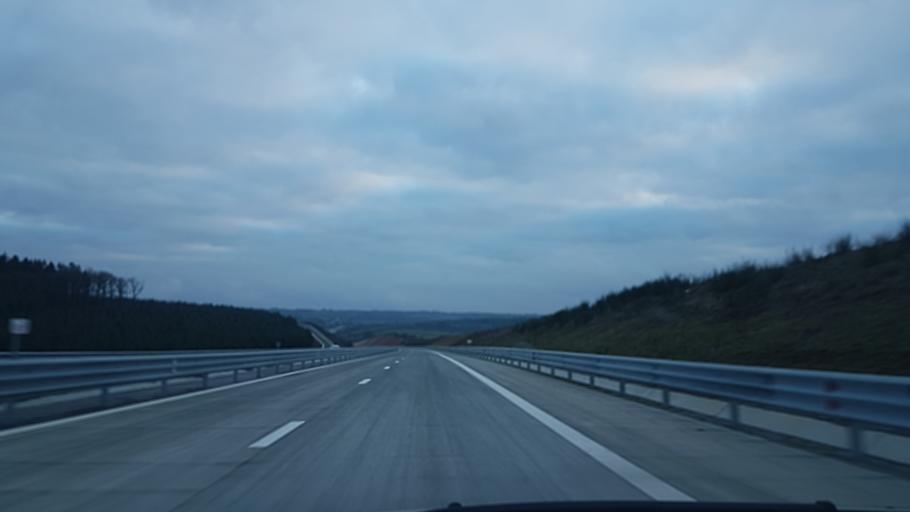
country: FR
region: Champagne-Ardenne
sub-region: Departement des Ardennes
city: Rocroi
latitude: 49.9884
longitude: 4.5410
